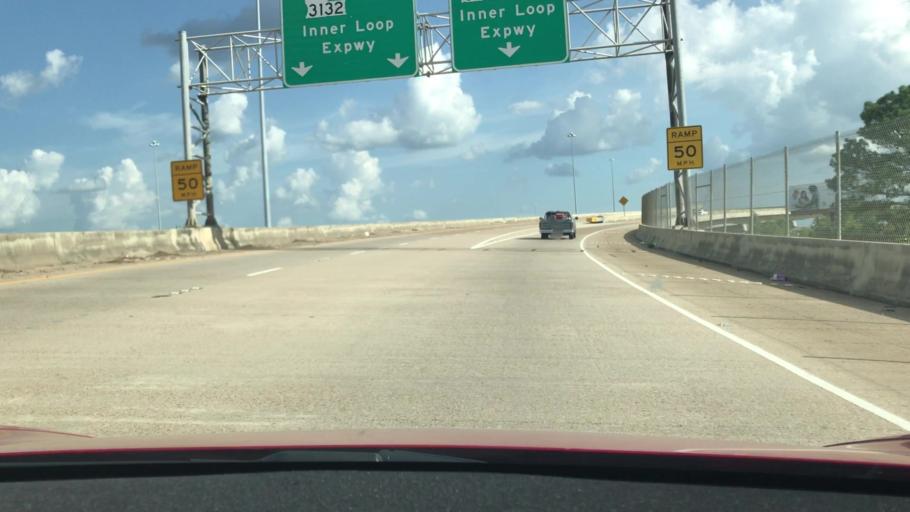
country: US
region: Louisiana
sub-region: Bossier Parish
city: Bossier City
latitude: 32.4232
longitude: -93.7500
